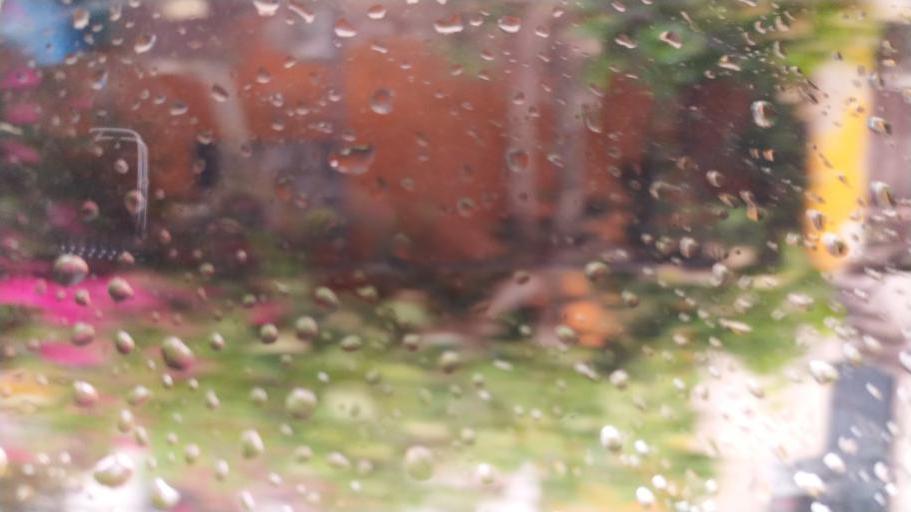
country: MX
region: Jalisco
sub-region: Zapopan
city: Zapopan
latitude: 20.7179
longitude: -103.3599
